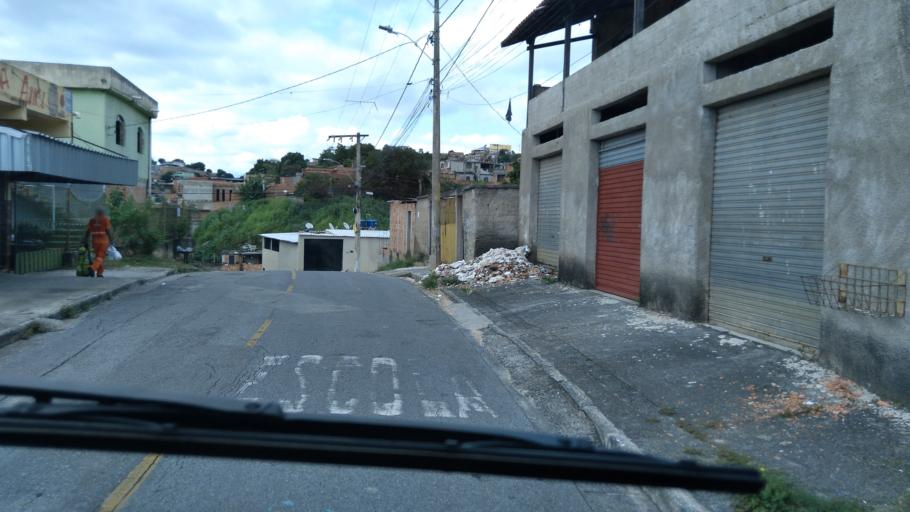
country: BR
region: Minas Gerais
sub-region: Santa Luzia
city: Santa Luzia
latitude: -19.8333
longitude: -43.8964
